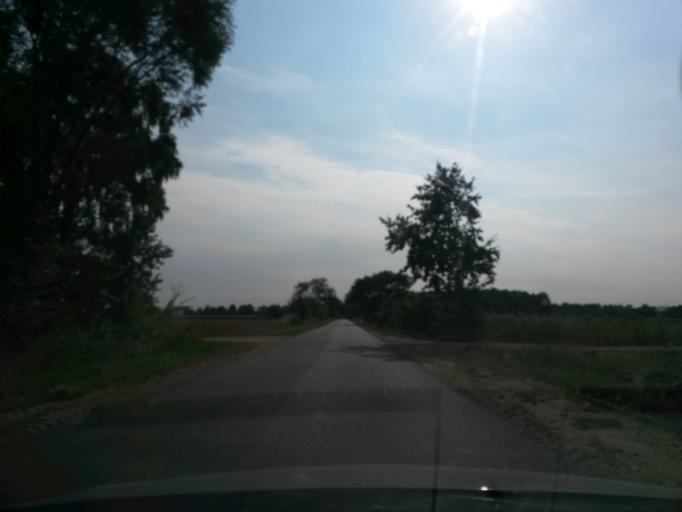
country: PL
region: Masovian Voivodeship
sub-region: Powiat sierpecki
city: Szczutowo
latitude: 52.9586
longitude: 19.6109
